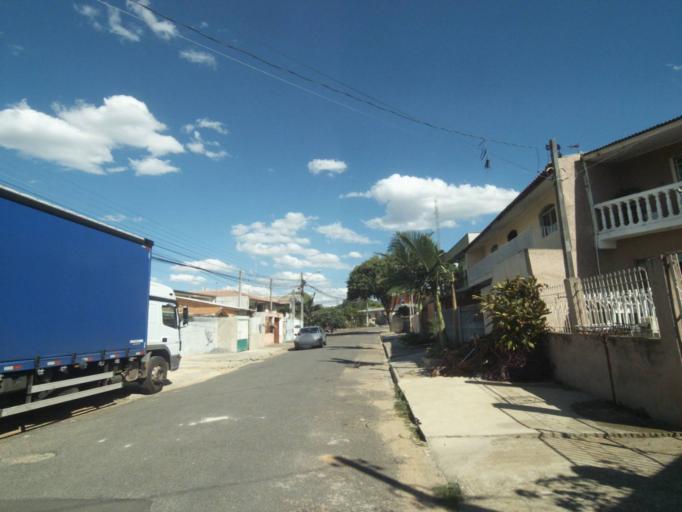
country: BR
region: Parana
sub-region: Curitiba
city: Curitiba
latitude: -25.4996
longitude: -49.3190
